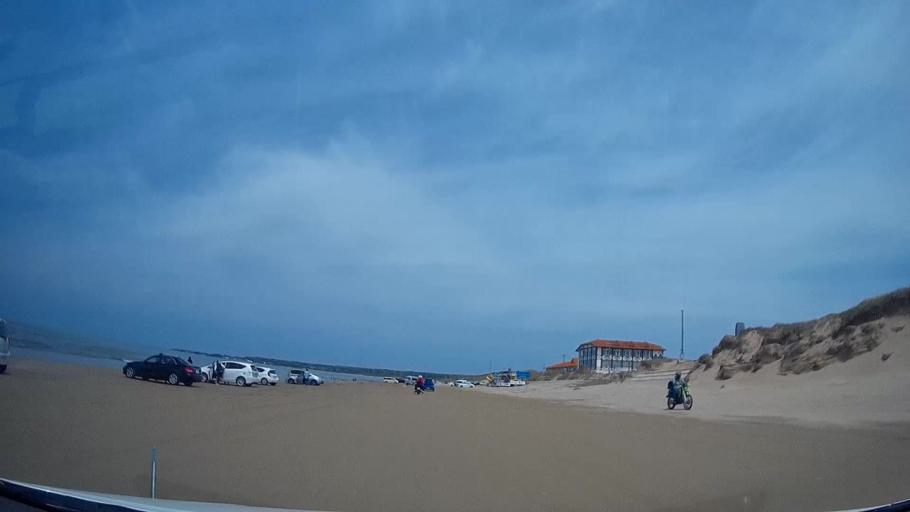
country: JP
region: Ishikawa
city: Hakui
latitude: 36.8918
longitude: 136.7655
